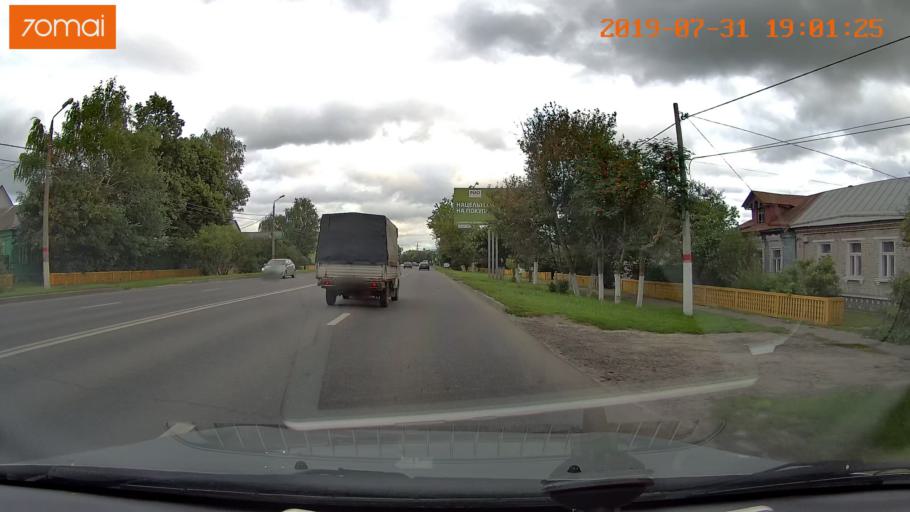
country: RU
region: Moskovskaya
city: Raduzhnyy
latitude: 55.1268
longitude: 38.7288
